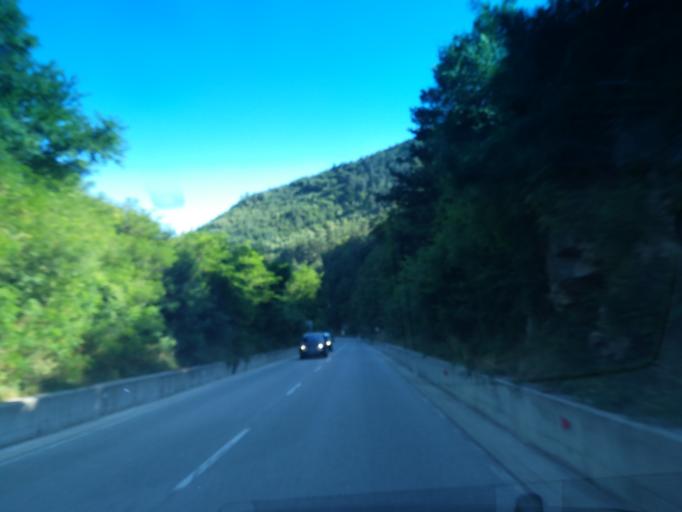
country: BG
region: Smolyan
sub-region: Obshtina Chepelare
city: Chepelare
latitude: 41.8380
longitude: 24.6796
